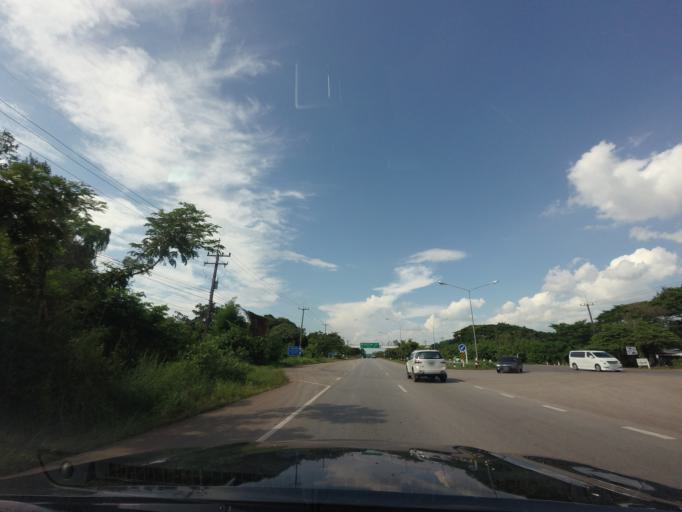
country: TH
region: Nong Khai
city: Sa Khrai
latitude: 17.6622
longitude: 102.7907
